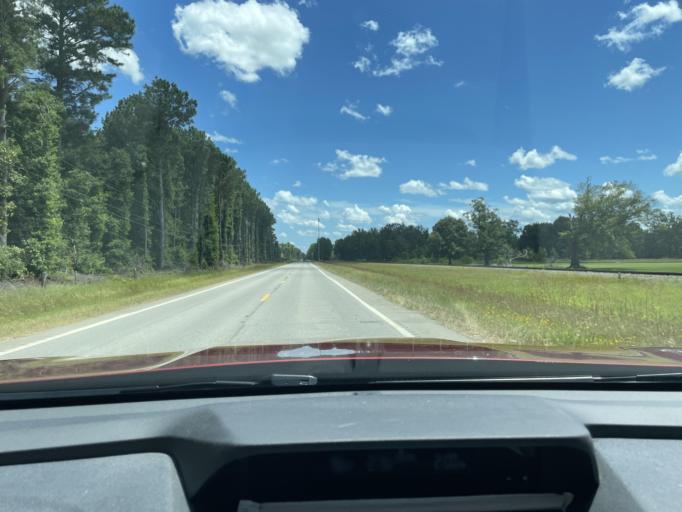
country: US
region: Arkansas
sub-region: Drew County
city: Monticello
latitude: 33.6156
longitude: -91.7442
